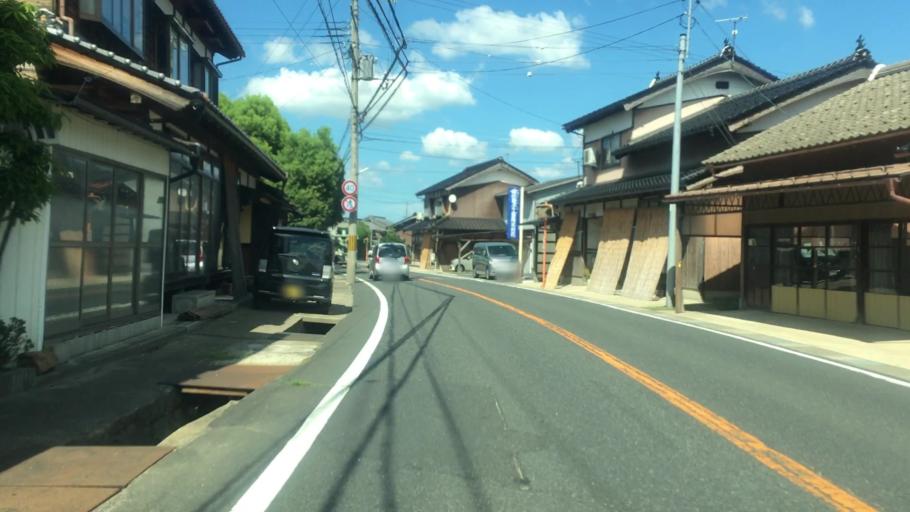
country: JP
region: Kyoto
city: Miyazu
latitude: 35.5914
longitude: 135.0402
